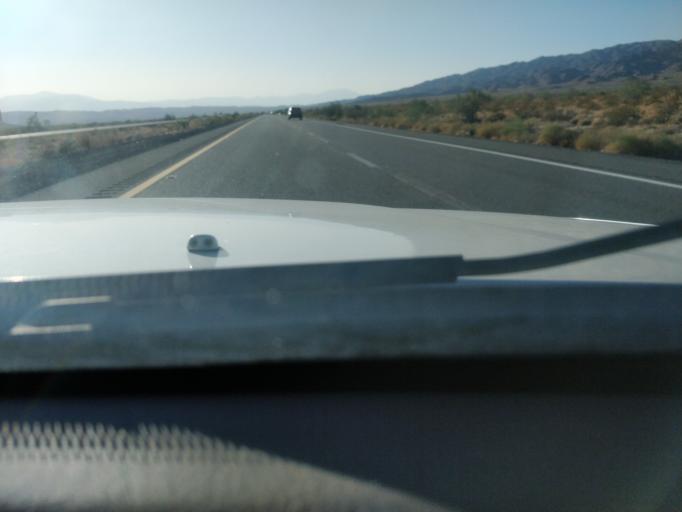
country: US
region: California
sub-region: Riverside County
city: Mecca
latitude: 33.6609
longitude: -115.8185
